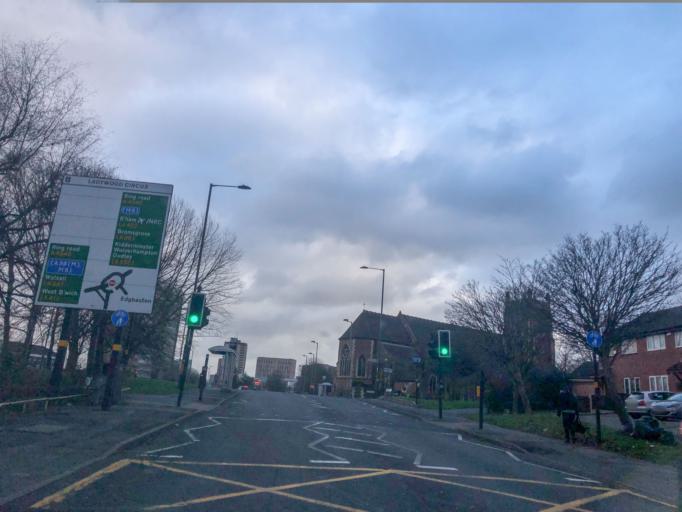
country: GB
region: England
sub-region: City and Borough of Birmingham
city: Hockley
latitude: 52.4786
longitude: -1.9284
